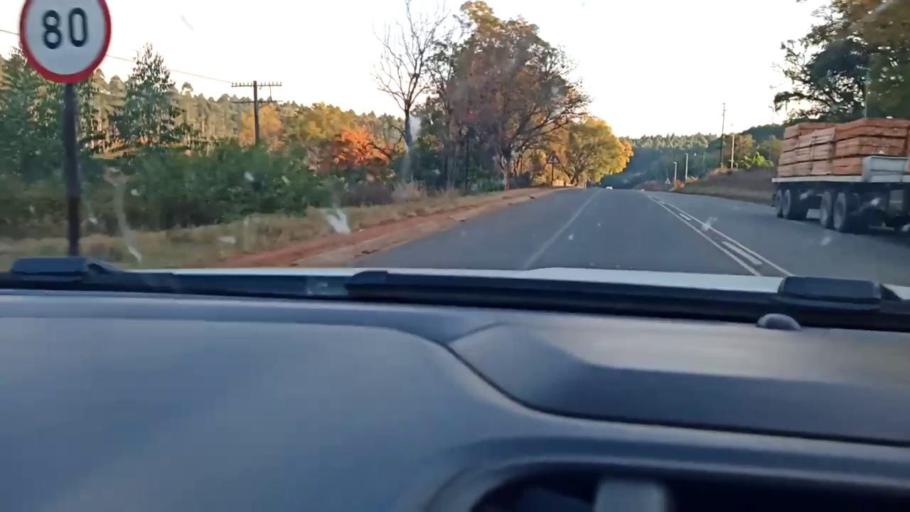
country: ZA
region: Limpopo
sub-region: Mopani District Municipality
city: Duiwelskloof
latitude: -23.7038
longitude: 30.1334
